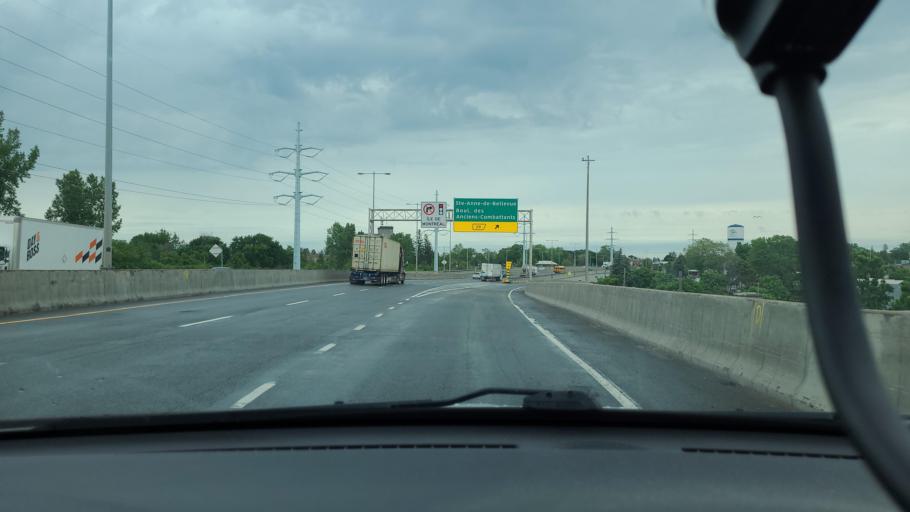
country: CA
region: Quebec
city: Sainte-Anne-de-Bellevue
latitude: 45.4044
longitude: -73.9545
